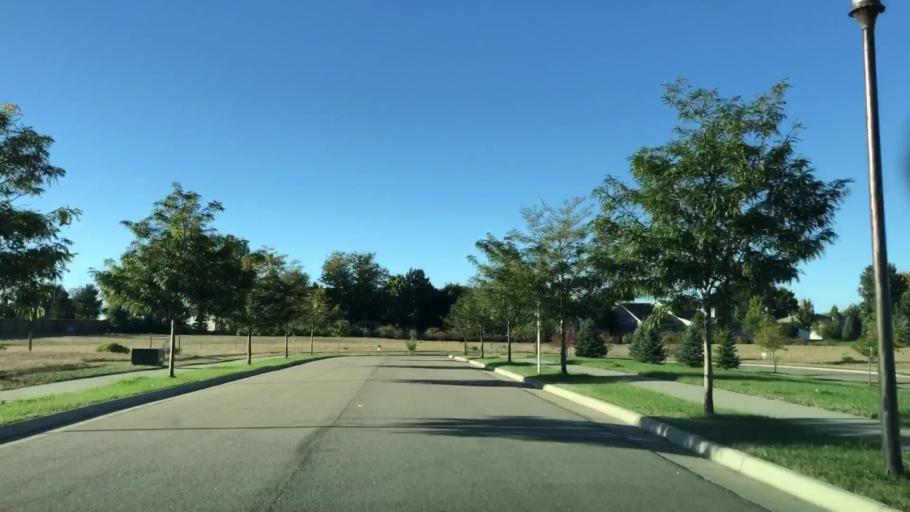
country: US
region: Colorado
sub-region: Larimer County
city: Loveland
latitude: 40.4324
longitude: -105.0214
